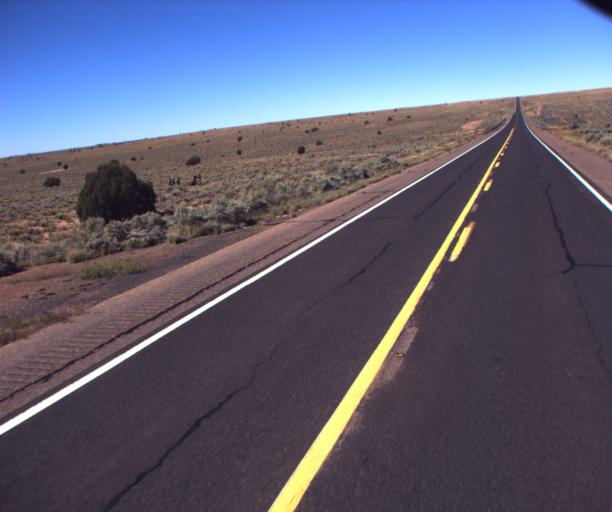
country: US
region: Arizona
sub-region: Navajo County
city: Snowflake
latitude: 34.6907
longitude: -109.7439
